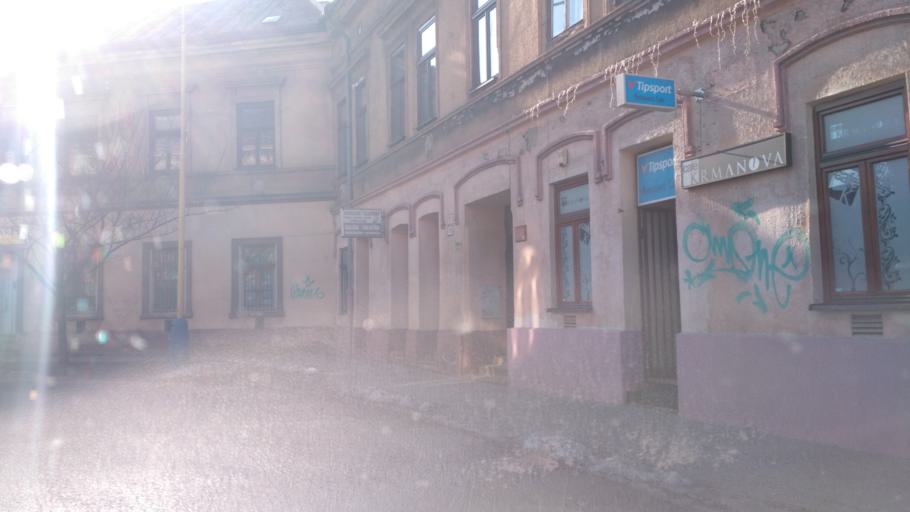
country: SK
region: Kosicky
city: Kosice
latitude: 48.7191
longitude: 21.2609
